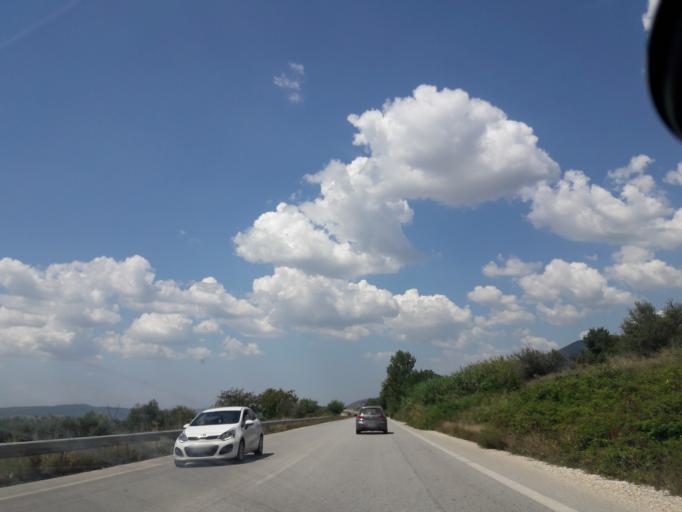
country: GR
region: Central Macedonia
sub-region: Nomos Chalkidikis
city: Galatista
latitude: 40.4617
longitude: 23.2798
